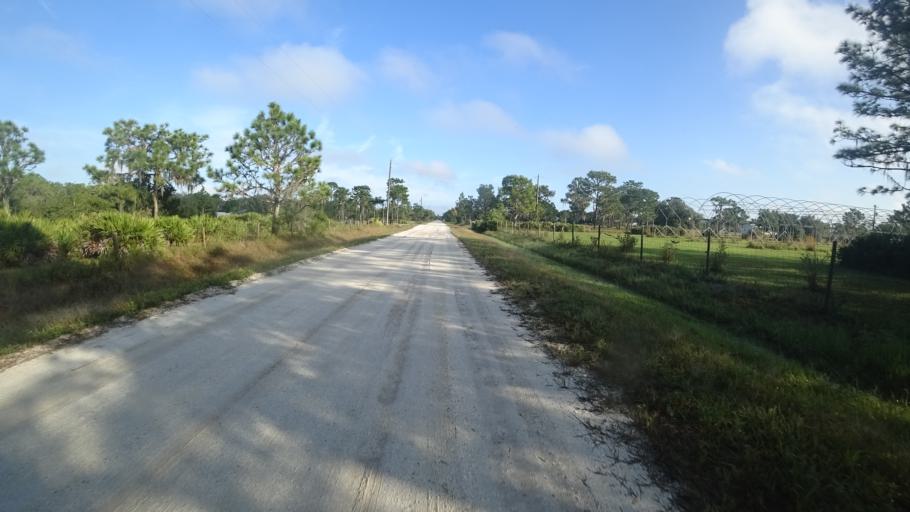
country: US
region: Florida
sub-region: Sarasota County
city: Fruitville
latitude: 27.4065
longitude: -82.2916
